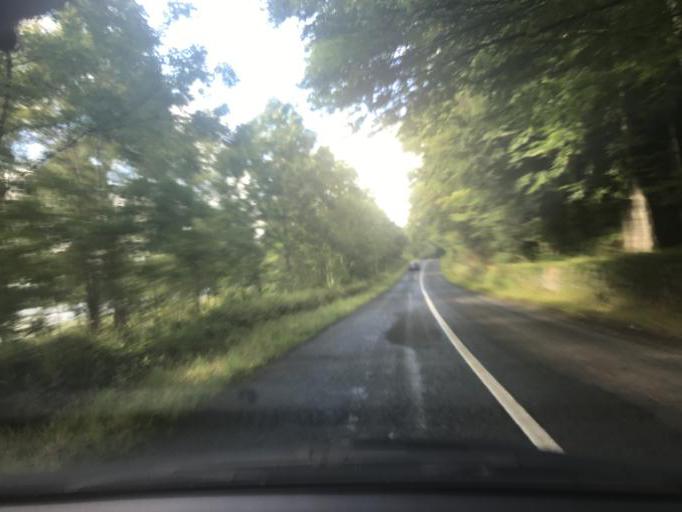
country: IE
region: Connaught
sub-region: Sligo
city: Collooney
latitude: 54.2039
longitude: -8.4634
